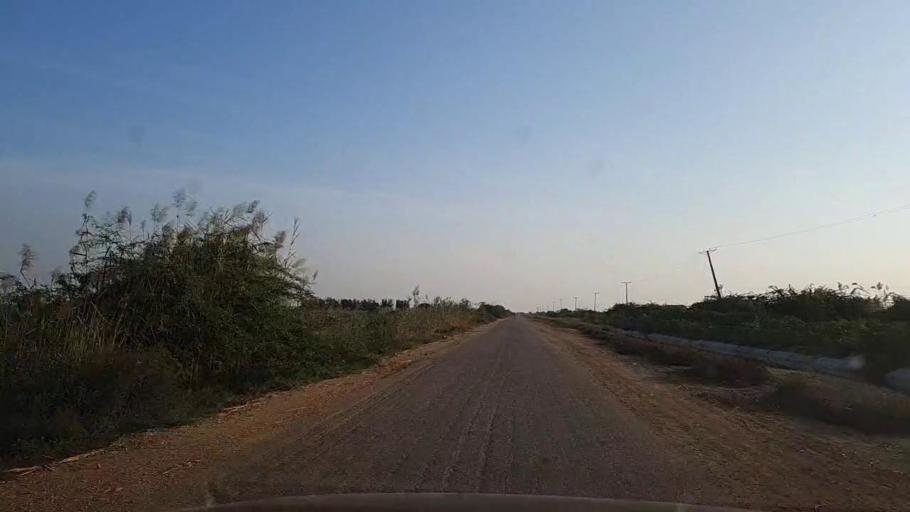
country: PK
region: Sindh
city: Thatta
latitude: 24.6473
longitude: 67.9124
